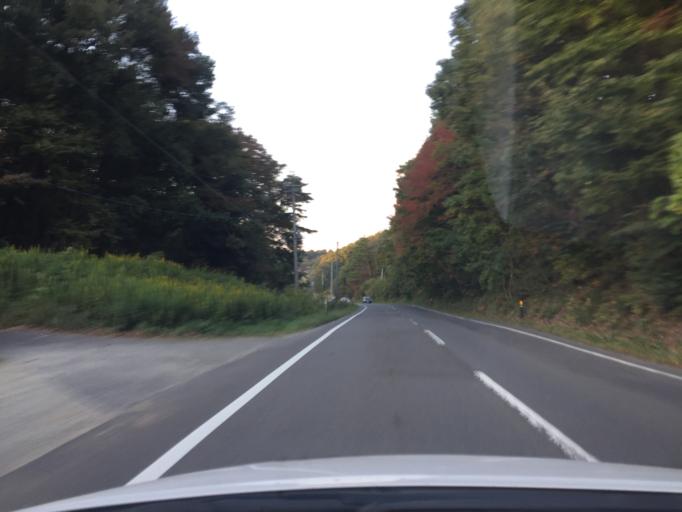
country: JP
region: Fukushima
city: Sukagawa
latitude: 37.3356
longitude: 140.4407
